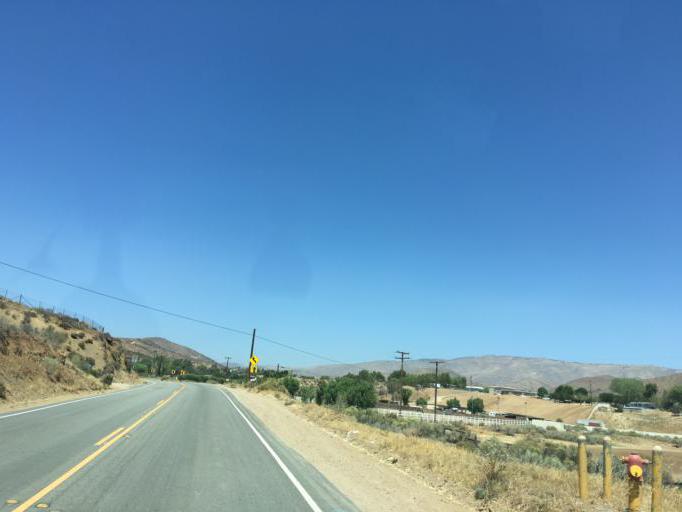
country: US
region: California
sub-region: Los Angeles County
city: Acton
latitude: 34.4806
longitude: -118.2085
